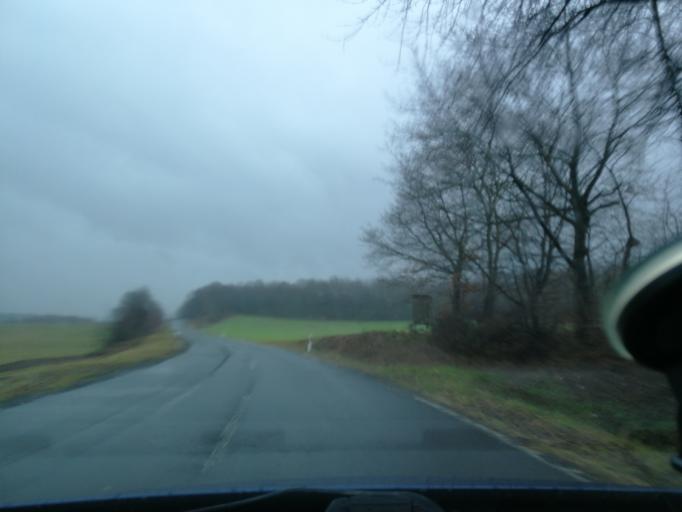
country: DE
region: Rheinland-Pfalz
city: Berglicht
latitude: 49.7824
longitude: 6.9776
